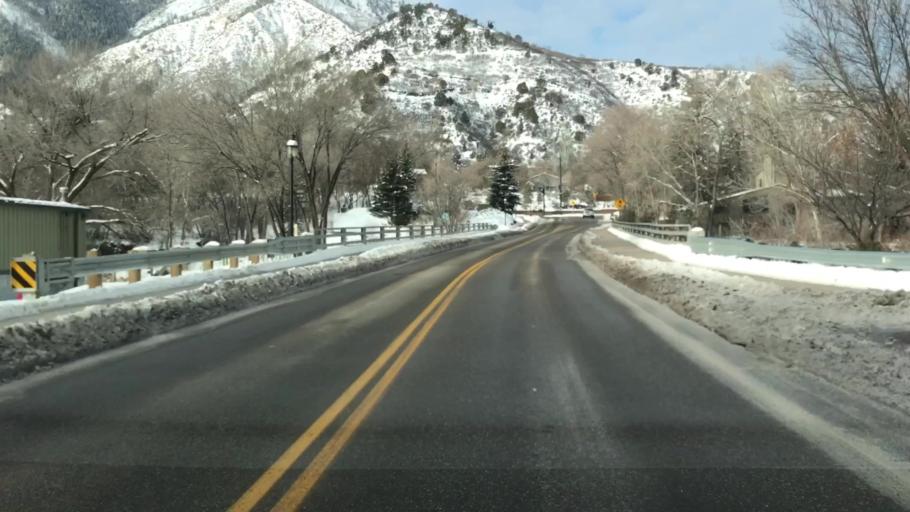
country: US
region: Colorado
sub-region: Garfield County
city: Glenwood Springs
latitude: 39.5468
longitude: -107.3299
